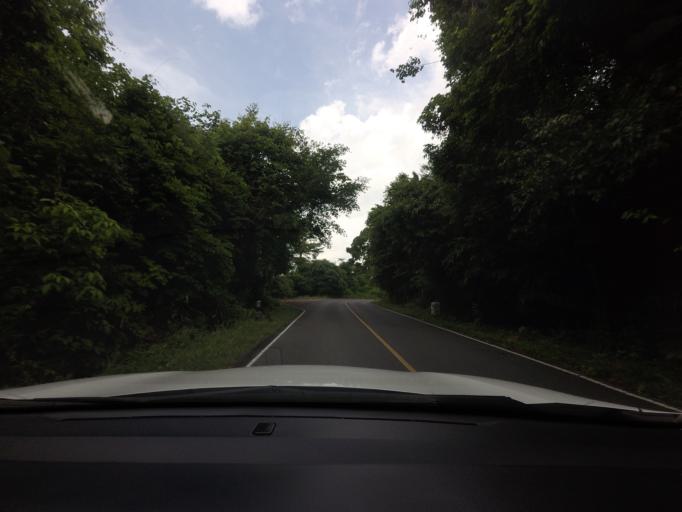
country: TH
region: Nakhon Nayok
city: Pak Phli
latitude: 14.2513
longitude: 101.3826
